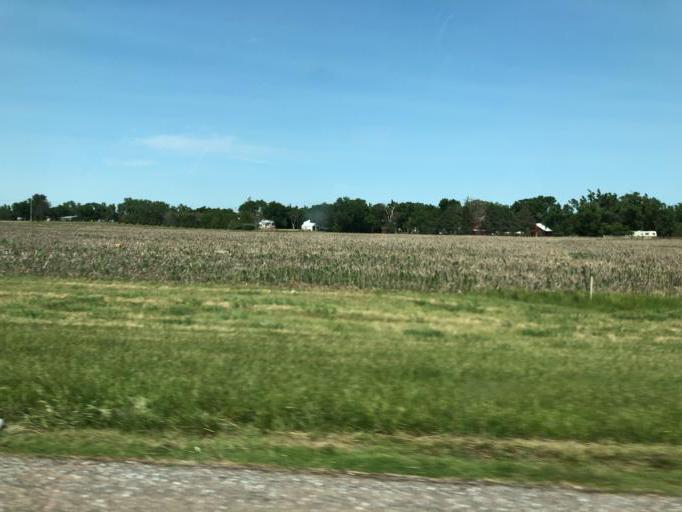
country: US
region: Nebraska
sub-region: Fillmore County
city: Geneva
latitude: 40.4127
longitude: -97.5923
